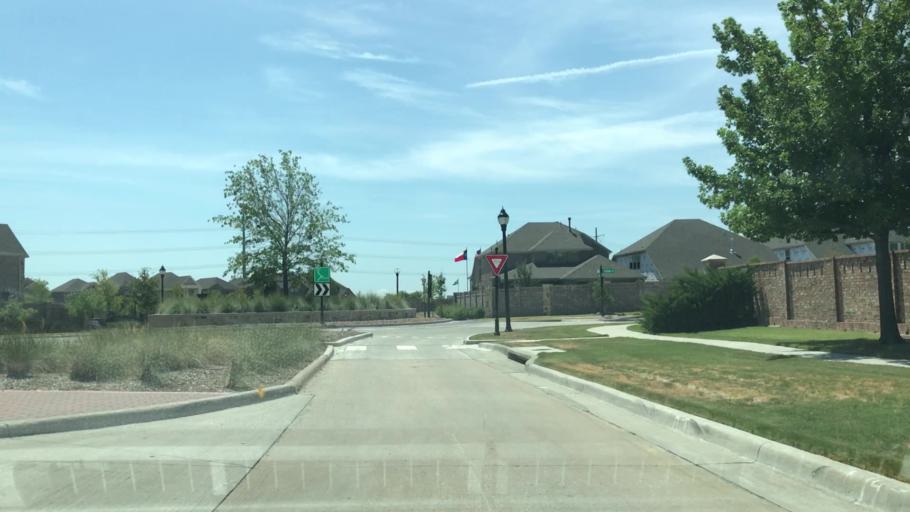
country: US
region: Texas
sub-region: Collin County
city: Allen
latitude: 33.1237
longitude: -96.6713
